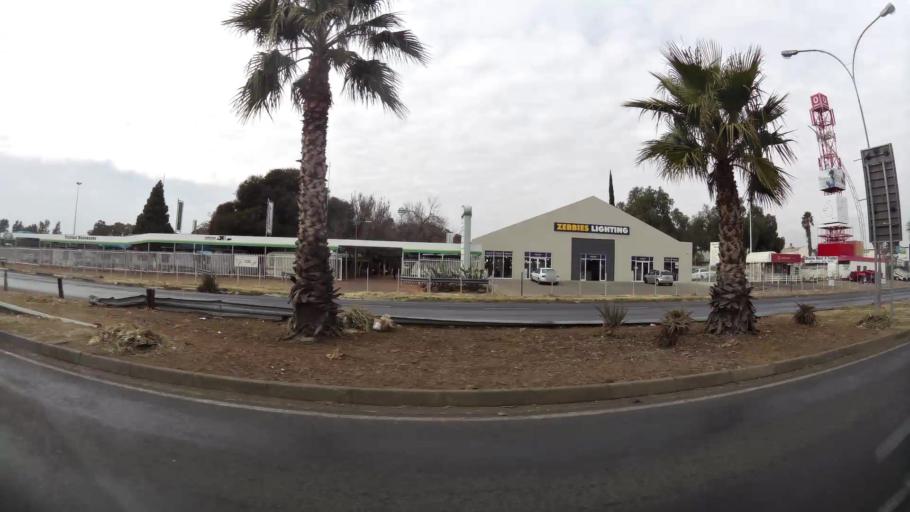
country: ZA
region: Orange Free State
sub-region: Mangaung Metropolitan Municipality
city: Bloemfontein
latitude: -29.1343
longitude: 26.2058
